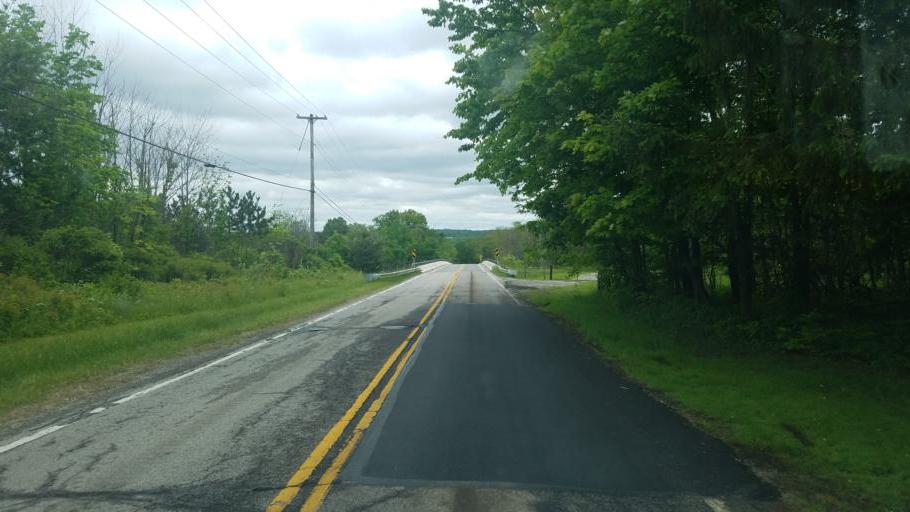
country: US
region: Ohio
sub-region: Summit County
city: Hudson
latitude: 41.2696
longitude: -81.4017
